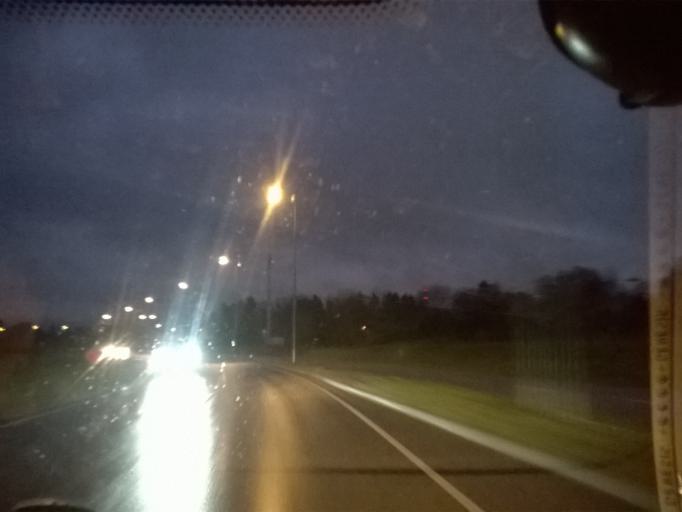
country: EE
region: Harju
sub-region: Viimsi vald
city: Viimsi
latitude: 59.4943
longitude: 24.8763
